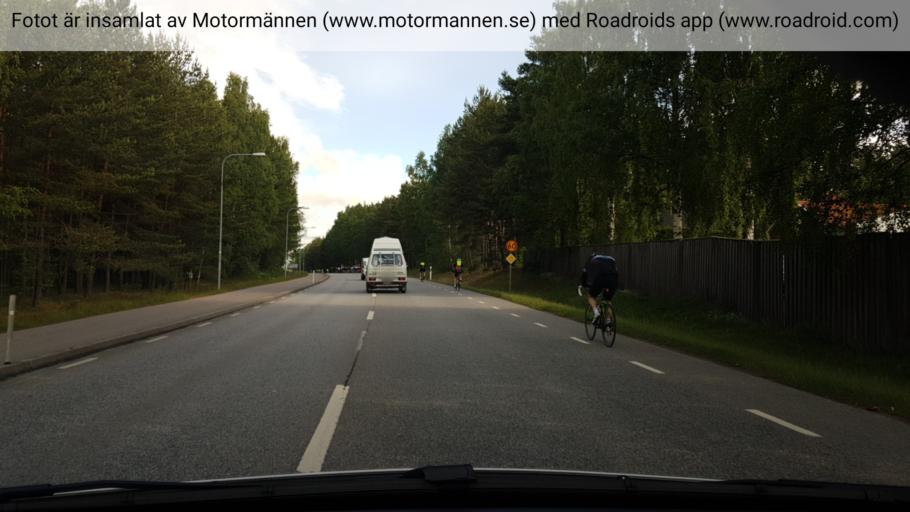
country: SE
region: Vaestra Goetaland
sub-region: Karlsborgs Kommun
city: Karlsborg
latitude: 58.5602
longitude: 14.5006
